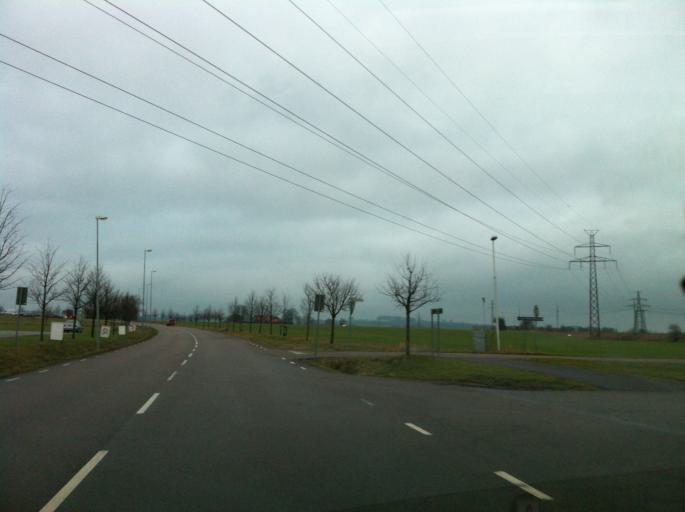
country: SE
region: Skane
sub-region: Landskrona
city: Asmundtorp
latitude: 55.8731
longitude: 12.8868
